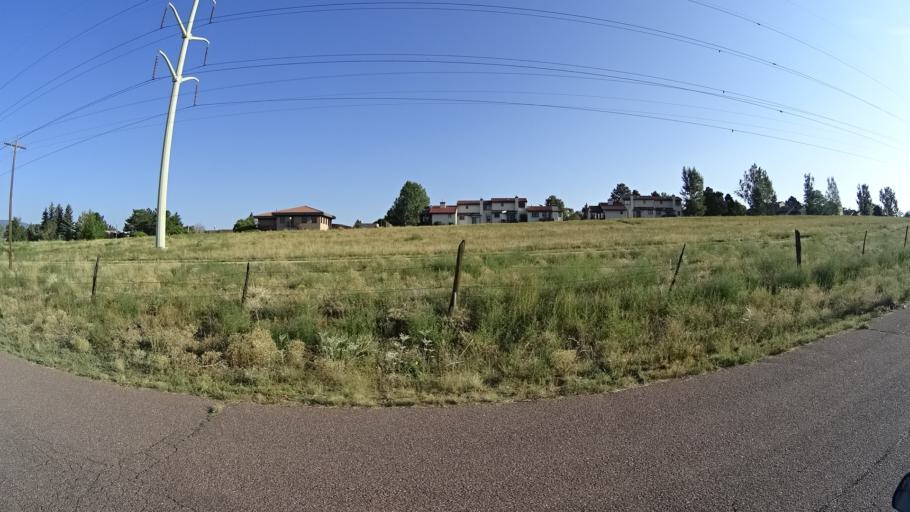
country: US
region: Colorado
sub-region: El Paso County
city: Black Forest
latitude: 38.9400
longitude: -104.7731
